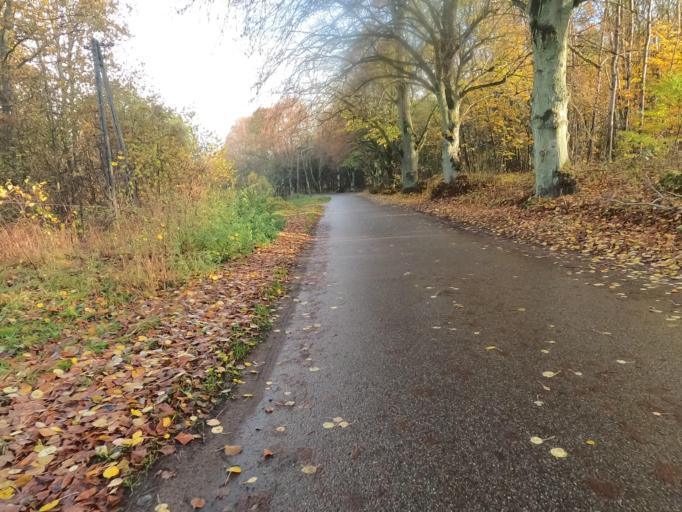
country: PL
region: West Pomeranian Voivodeship
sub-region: Powiat szczecinecki
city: Borne Sulinowo
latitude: 53.5315
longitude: 16.4711
